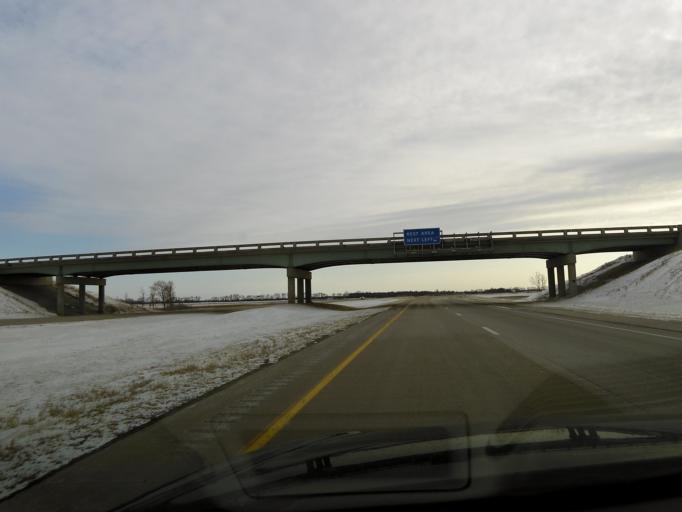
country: US
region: North Dakota
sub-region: Walsh County
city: Grafton
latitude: 48.4711
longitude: -97.1906
